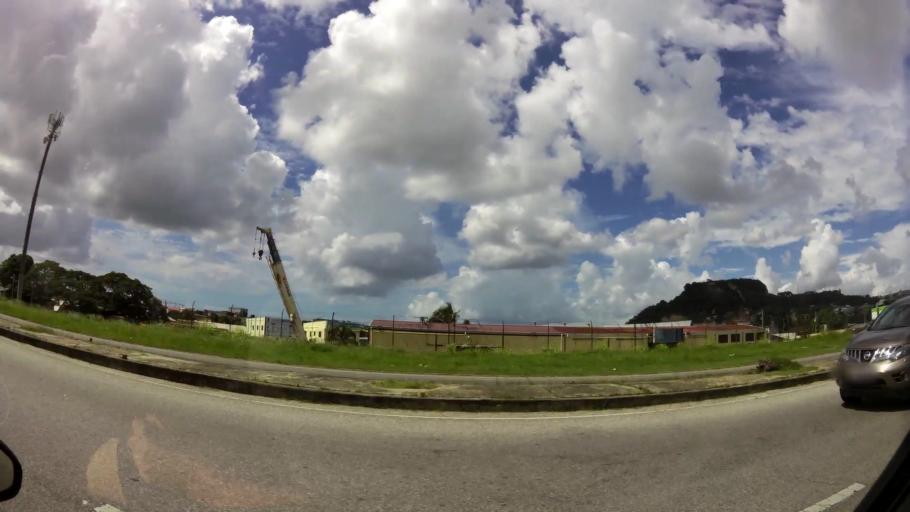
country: TT
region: City of San Fernando
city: Mon Repos
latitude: 10.2701
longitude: -61.4557
